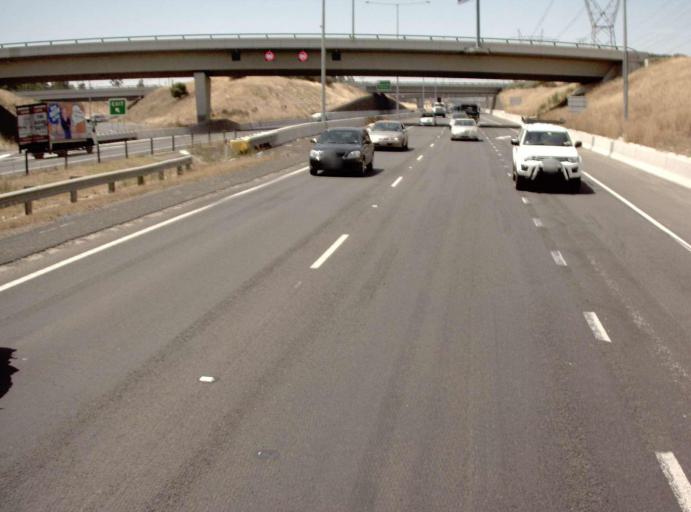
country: AU
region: Victoria
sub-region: Moonee Valley
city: Keilor East
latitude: -37.7295
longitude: 144.8576
